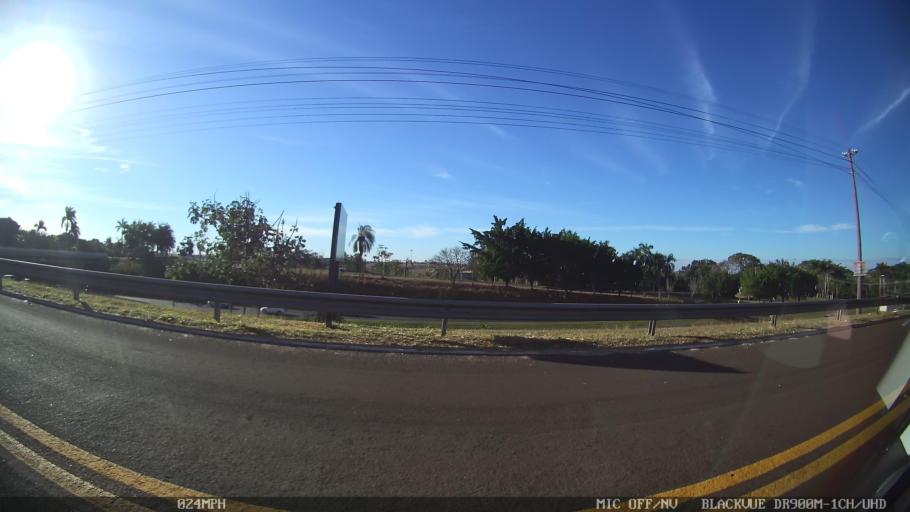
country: BR
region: Sao Paulo
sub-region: Sao Jose Do Rio Preto
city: Sao Jose do Rio Preto
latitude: -20.8165
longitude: -49.4483
